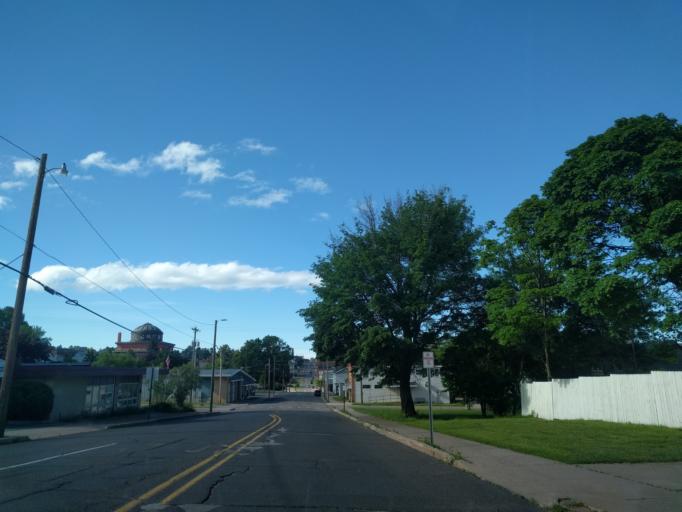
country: US
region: Michigan
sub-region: Marquette County
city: Marquette
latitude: 46.5394
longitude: -87.3966
